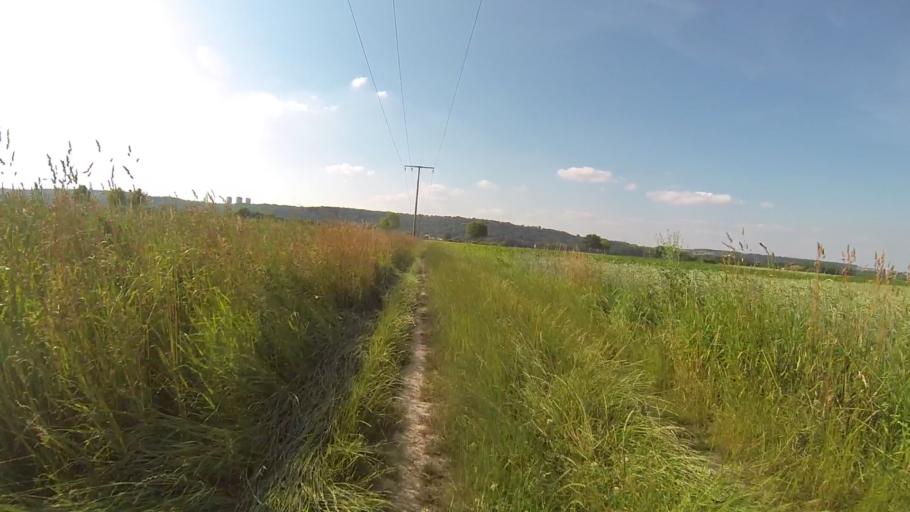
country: DE
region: Bavaria
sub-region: Swabia
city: Neu-Ulm
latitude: 48.4175
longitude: 10.0410
